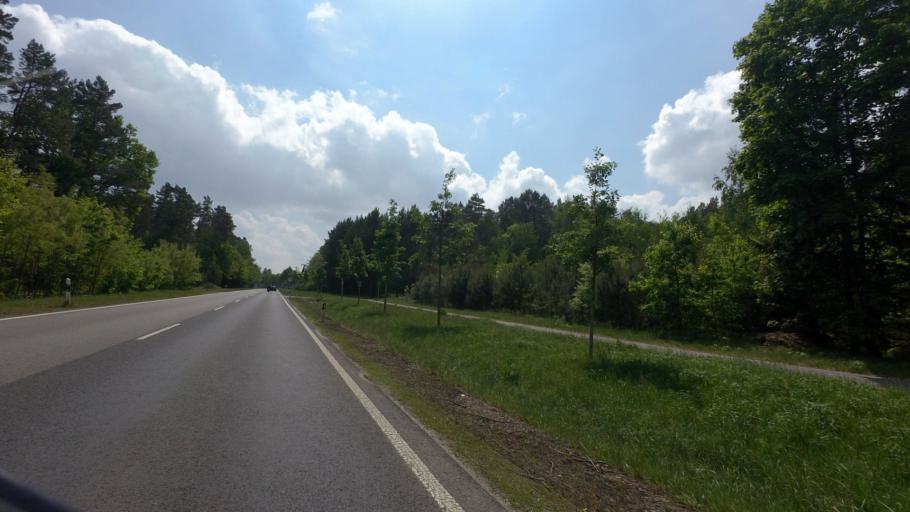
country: DE
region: Saxony
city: Weisskeissel
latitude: 51.4784
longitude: 14.7226
